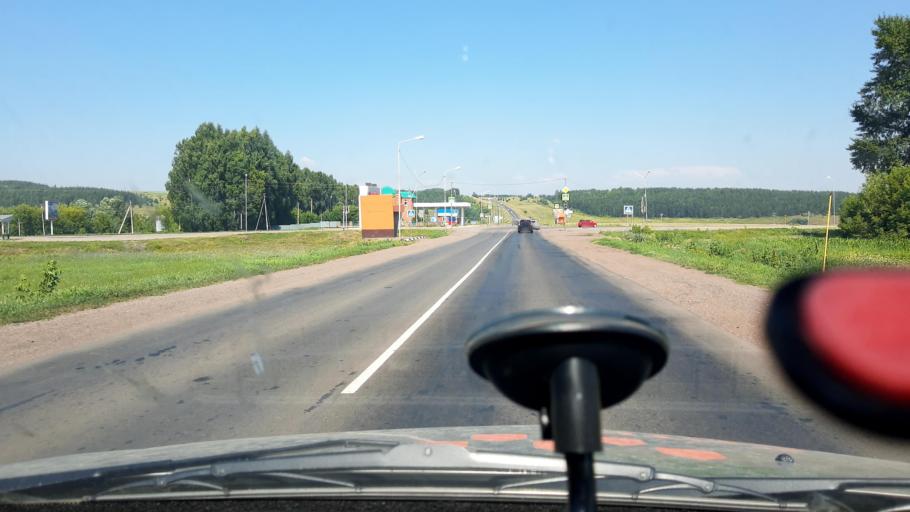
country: RU
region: Bashkortostan
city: Chekmagush
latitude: 55.1294
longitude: 54.6831
